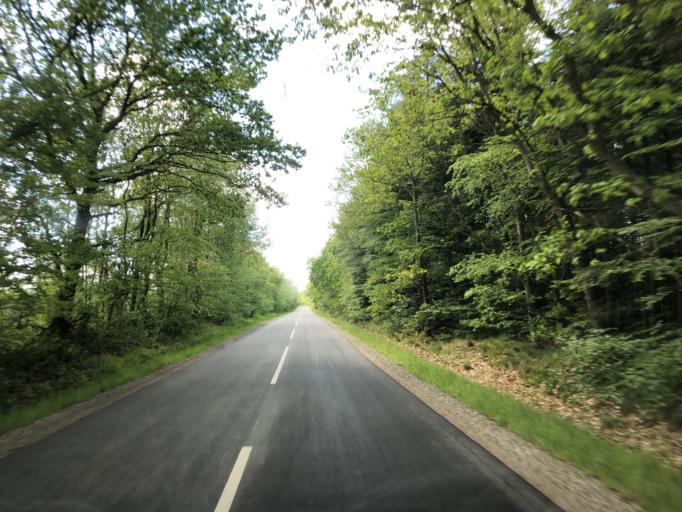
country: DK
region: Central Jutland
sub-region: Ringkobing-Skjern Kommune
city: Tarm
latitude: 55.9407
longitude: 8.5630
